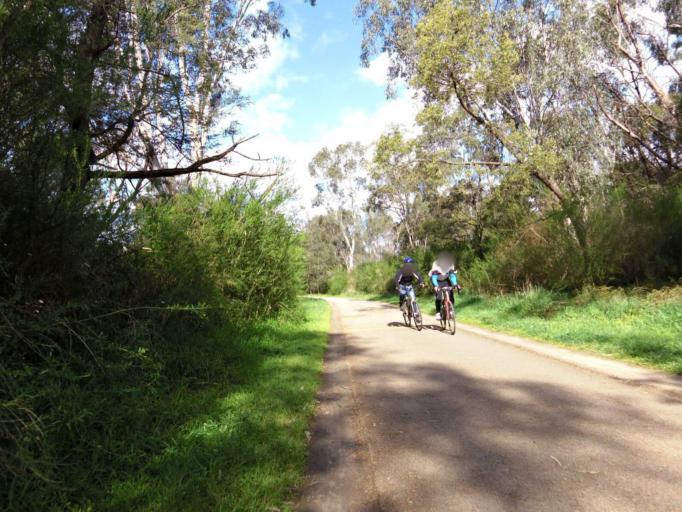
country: AU
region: Victoria
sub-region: Banyule
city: Viewbank
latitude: -37.7505
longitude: 145.1002
